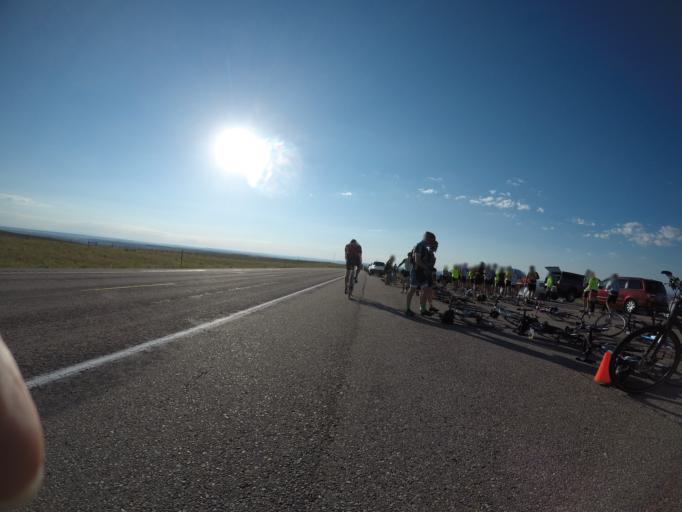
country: US
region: Wyoming
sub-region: Lincoln County
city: Kemmerer
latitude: 41.8870
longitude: -110.3855
